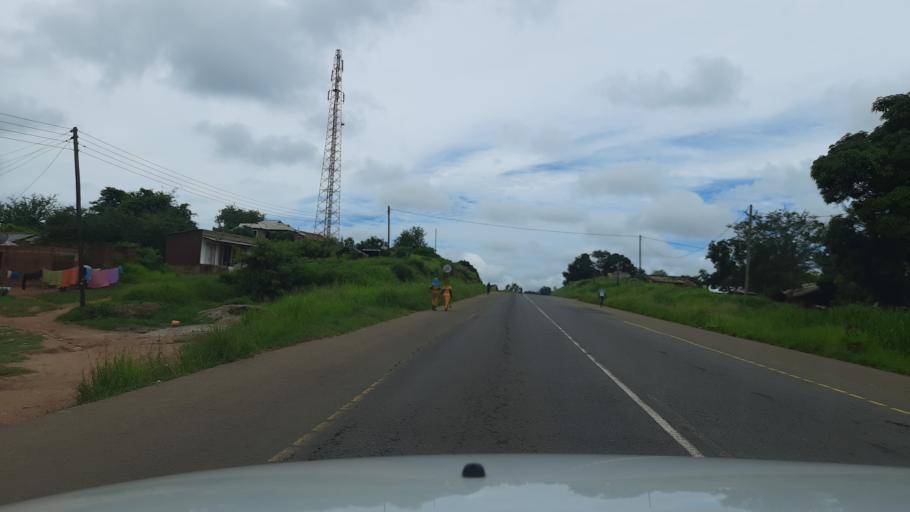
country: TZ
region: Pwani
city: Lugoba
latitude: -6.0772
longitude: 38.2433
